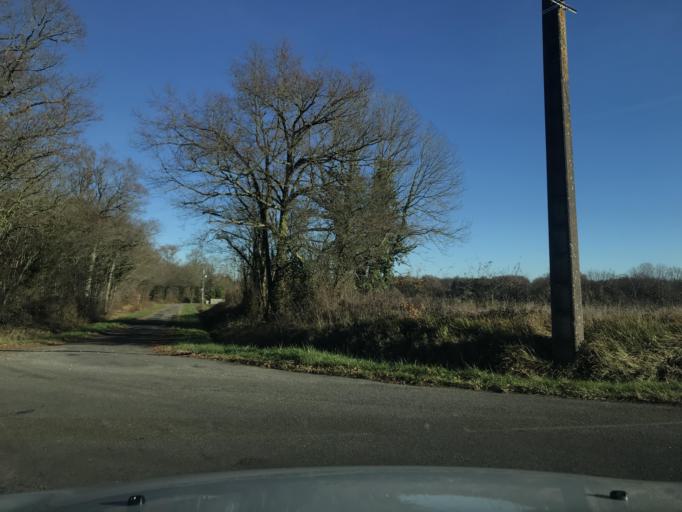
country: FR
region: Poitou-Charentes
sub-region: Departement de la Charente
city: Saint-Claud
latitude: 45.8558
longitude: 0.5076
